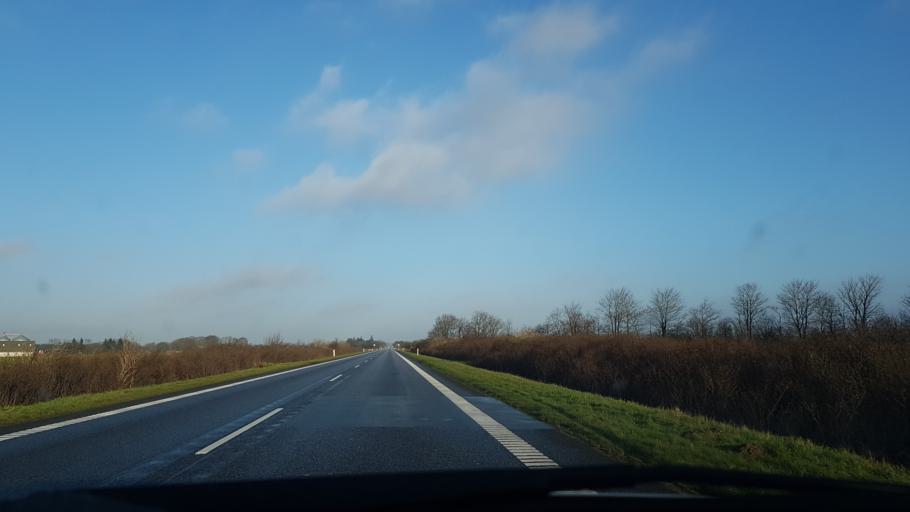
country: DK
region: South Denmark
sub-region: Tonder Kommune
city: Toftlund
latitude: 55.2242
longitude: 9.1114
